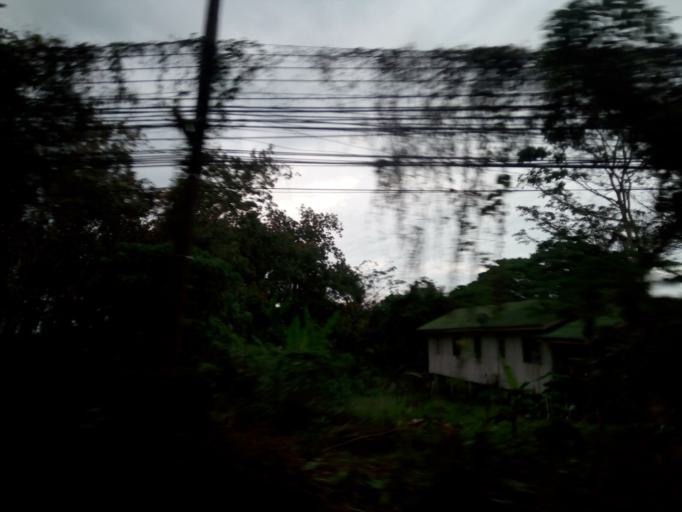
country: TH
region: Phuket
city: Thalang
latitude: 8.0688
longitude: 98.3937
